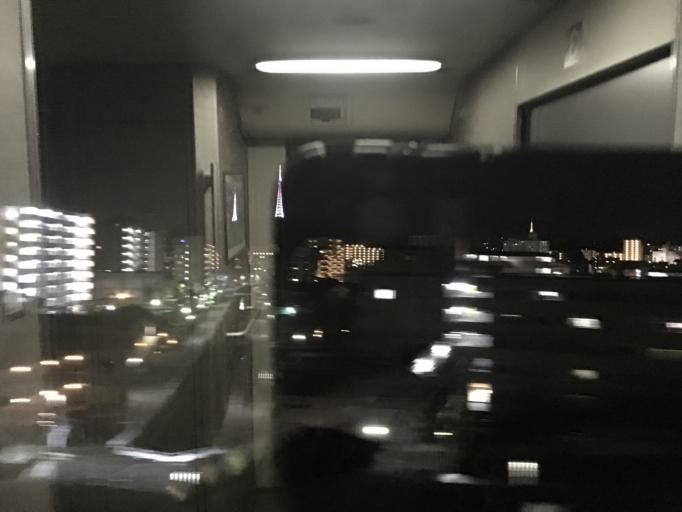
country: JP
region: Miyagi
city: Sendai
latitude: 38.2444
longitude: 140.8929
